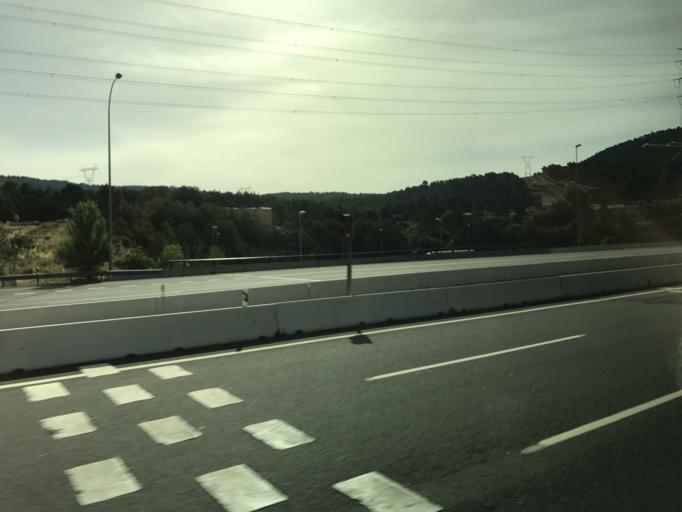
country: ES
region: Castille and Leon
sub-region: Provincia de Segovia
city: Otero de Herreros
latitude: 40.7289
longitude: -4.1942
